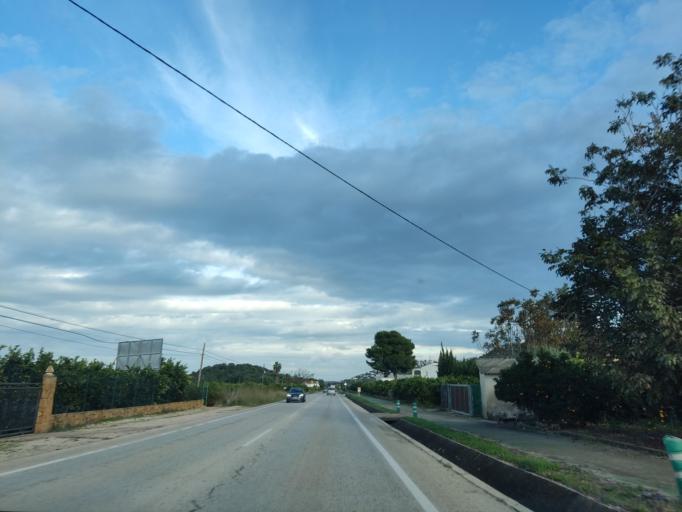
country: ES
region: Valencia
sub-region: Provincia de Alicante
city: Pego
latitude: 38.8477
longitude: -0.0820
